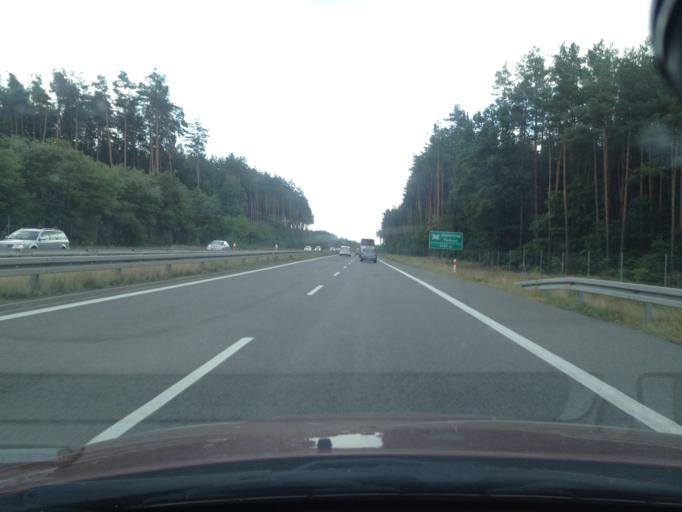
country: PL
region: West Pomeranian Voivodeship
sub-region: Powiat goleniowski
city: Goleniow
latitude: 53.6117
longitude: 14.8185
